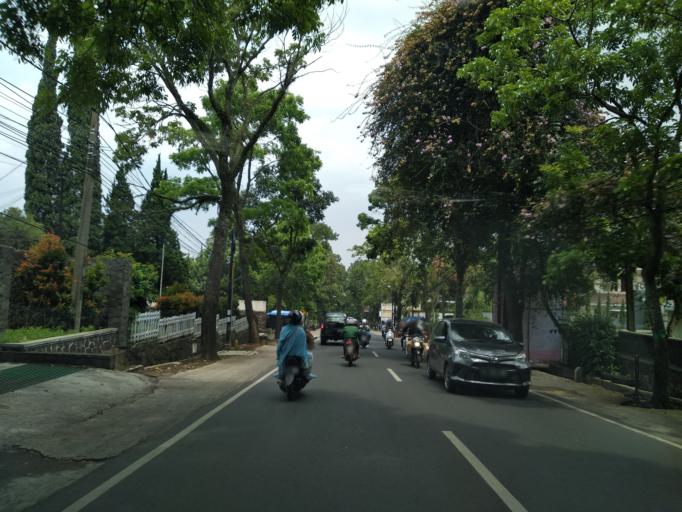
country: ID
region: West Java
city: Lembang
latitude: -6.8537
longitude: 107.5962
